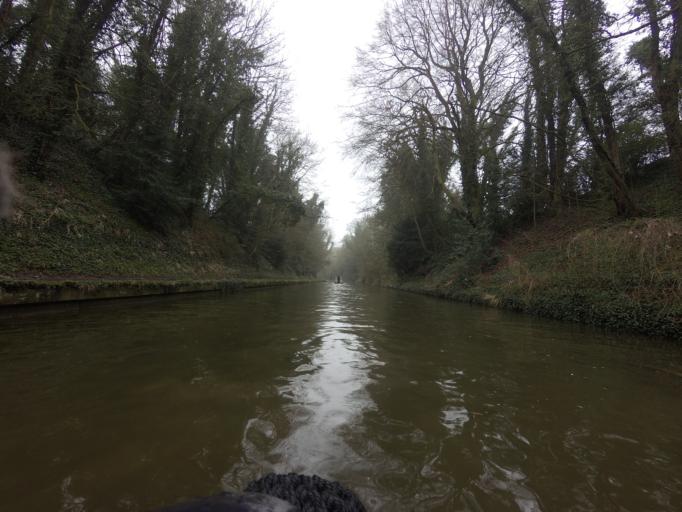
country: GB
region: England
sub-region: Hertfordshire
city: Tring
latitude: 51.8030
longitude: -0.6352
